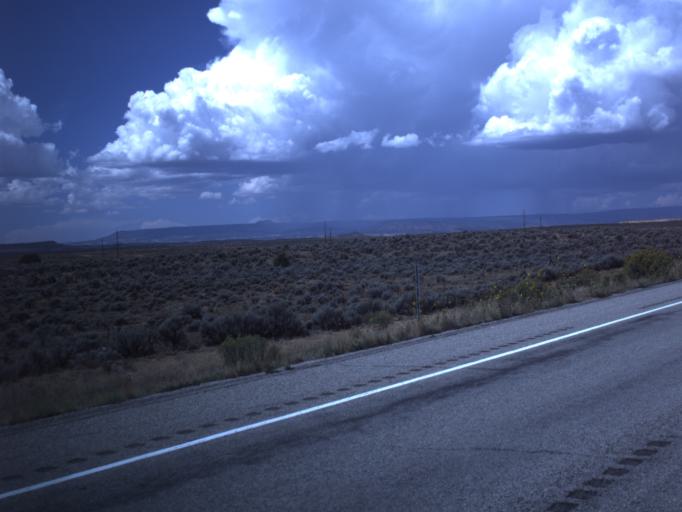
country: US
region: Utah
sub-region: San Juan County
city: Blanding
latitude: 37.5108
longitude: -109.4920
